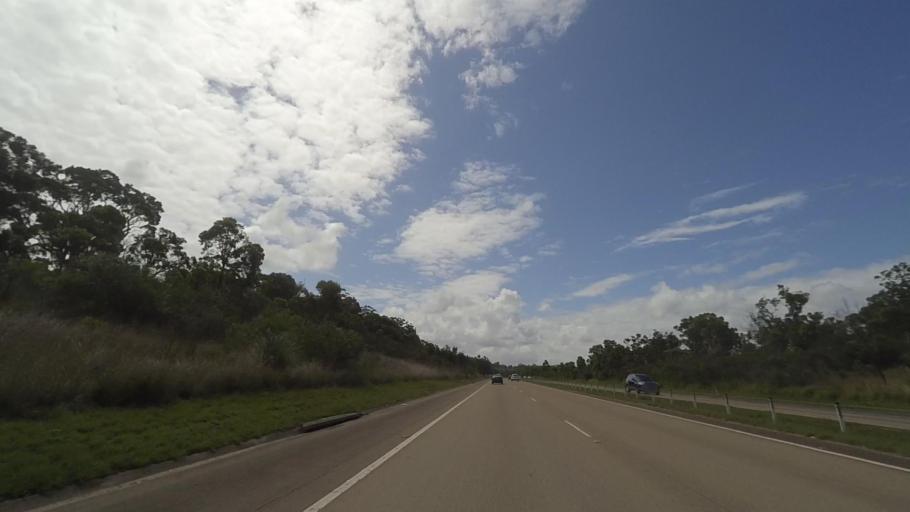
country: AU
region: New South Wales
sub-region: Lake Macquarie Shire
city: Windale
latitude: -32.9871
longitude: 151.6854
